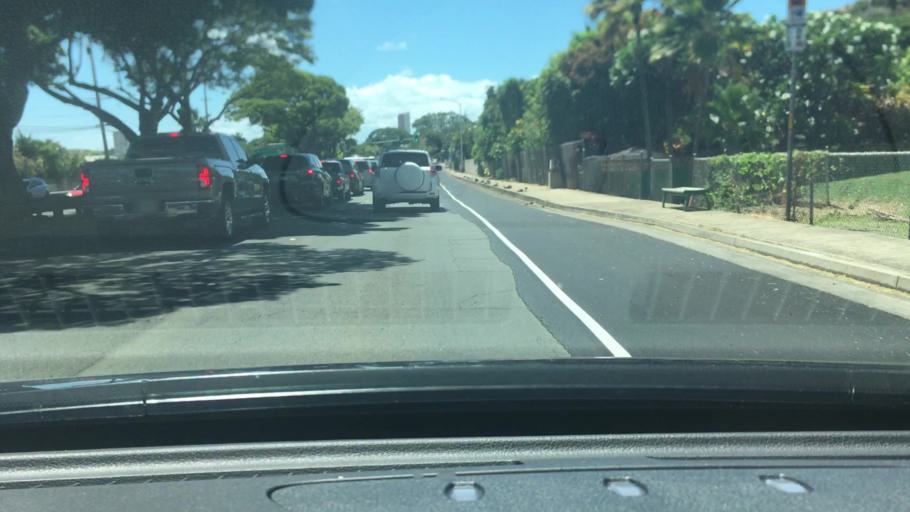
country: US
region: Hawaii
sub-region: Honolulu County
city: Waimanalo
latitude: 21.2768
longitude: -157.7703
